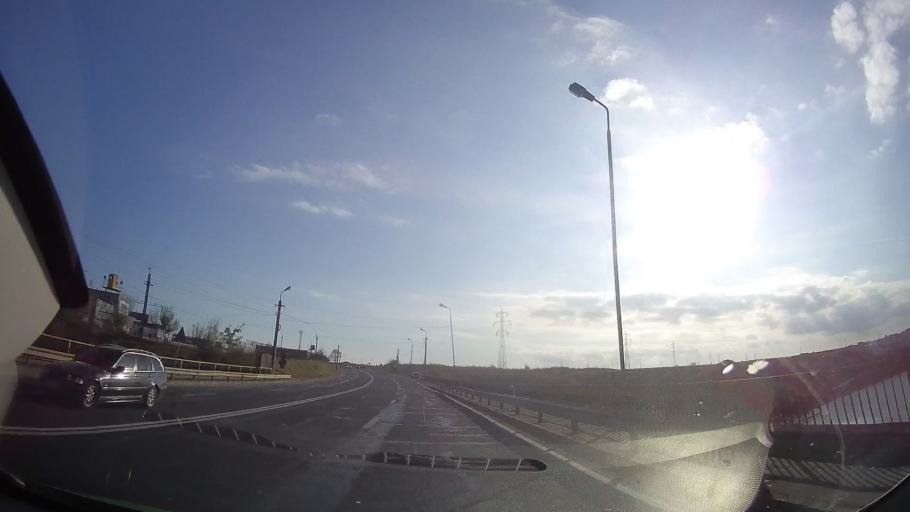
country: RO
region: Constanta
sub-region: Municipiul Mangalia
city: Mangalia
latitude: 43.8001
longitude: 28.5592
